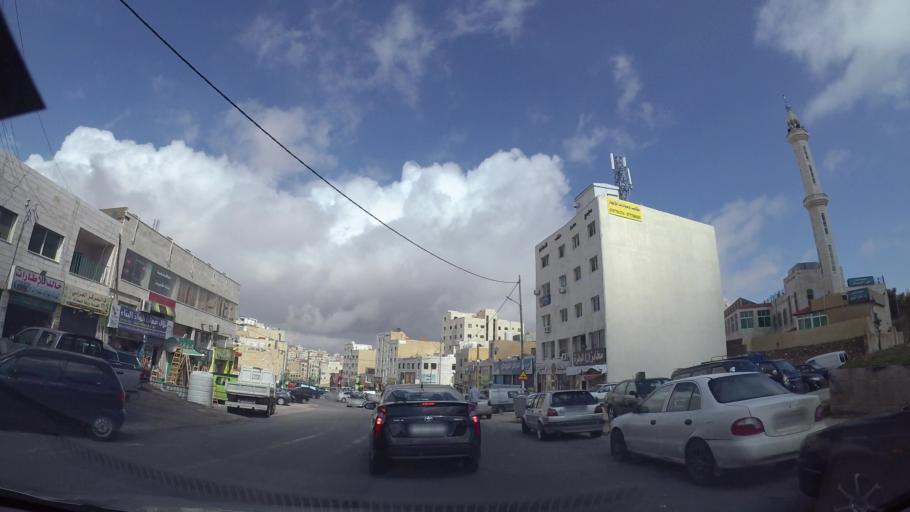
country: JO
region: Amman
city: Al Jubayhah
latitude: 32.0593
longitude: 35.8768
